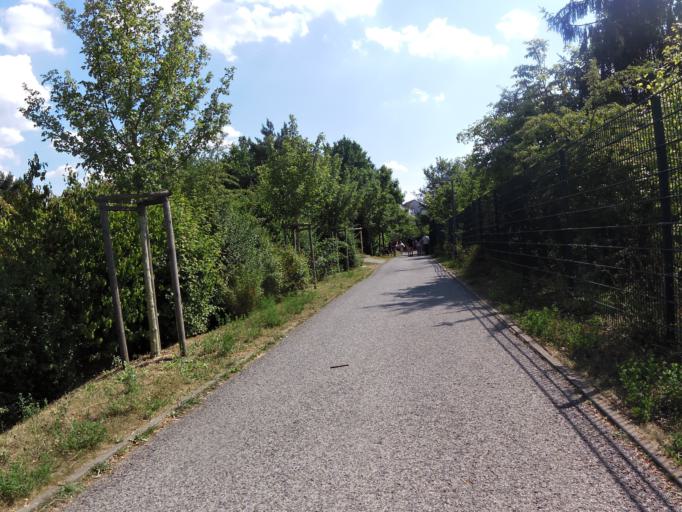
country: DE
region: Bavaria
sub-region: Regierungsbezirk Unterfranken
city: Randersacker
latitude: 49.7440
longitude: 9.9576
